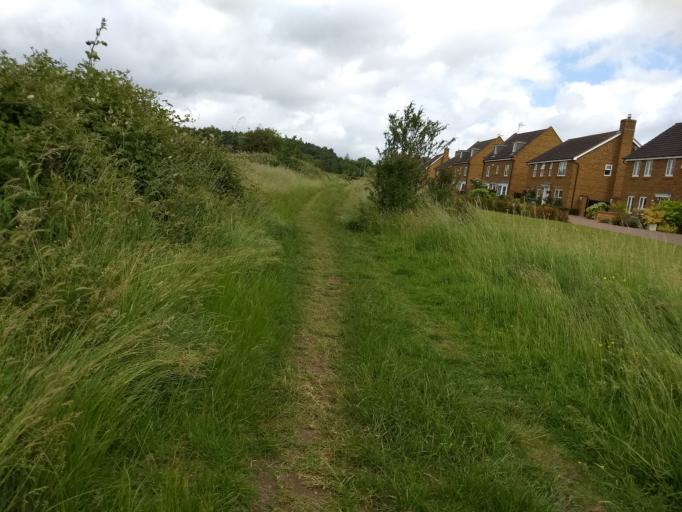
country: GB
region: England
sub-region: Milton Keynes
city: Shenley Church End
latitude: 52.0064
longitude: -0.8121
